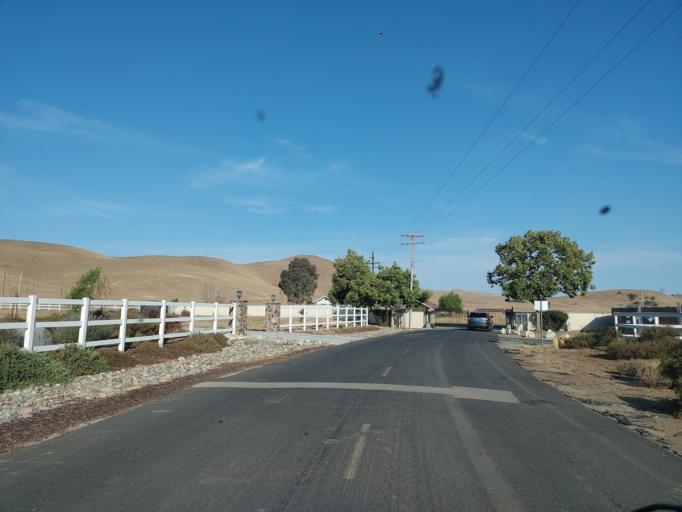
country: US
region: California
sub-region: San Benito County
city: Ridgemark
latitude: 36.7906
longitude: -121.3142
